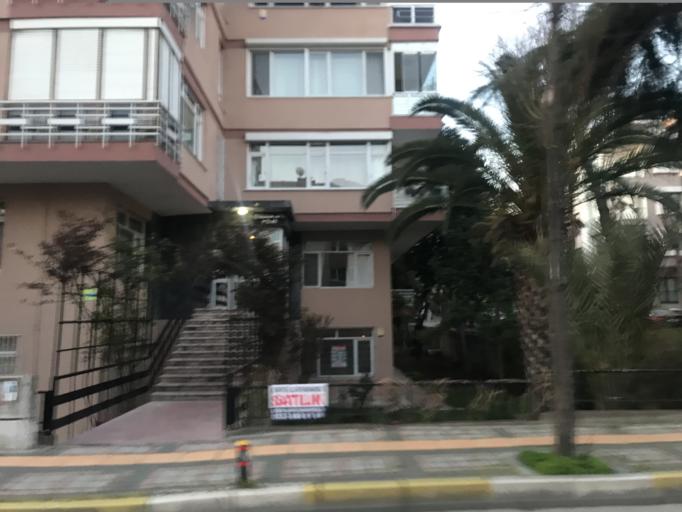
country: TR
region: Istanbul
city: Bahcelievler
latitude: 40.9607
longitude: 28.8325
